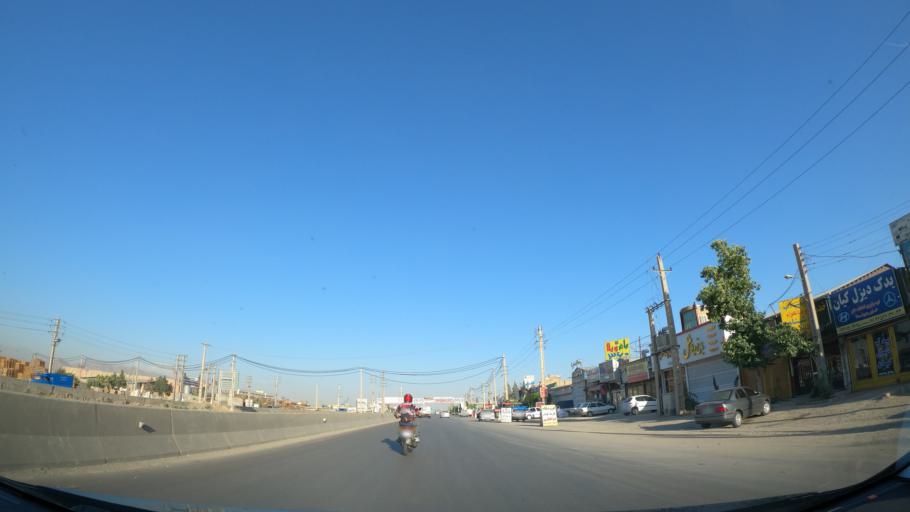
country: IR
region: Alborz
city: Hashtgerd
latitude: 35.9184
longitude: 50.7520
